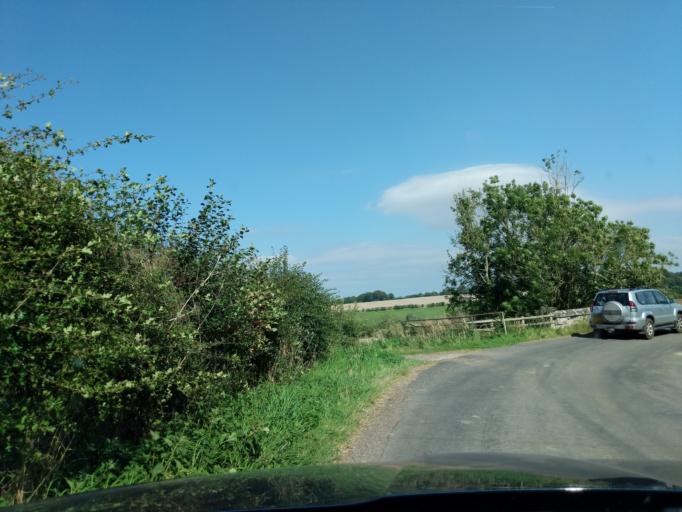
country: GB
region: Scotland
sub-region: The Scottish Borders
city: Coldstream
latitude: 55.6733
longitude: -2.1743
